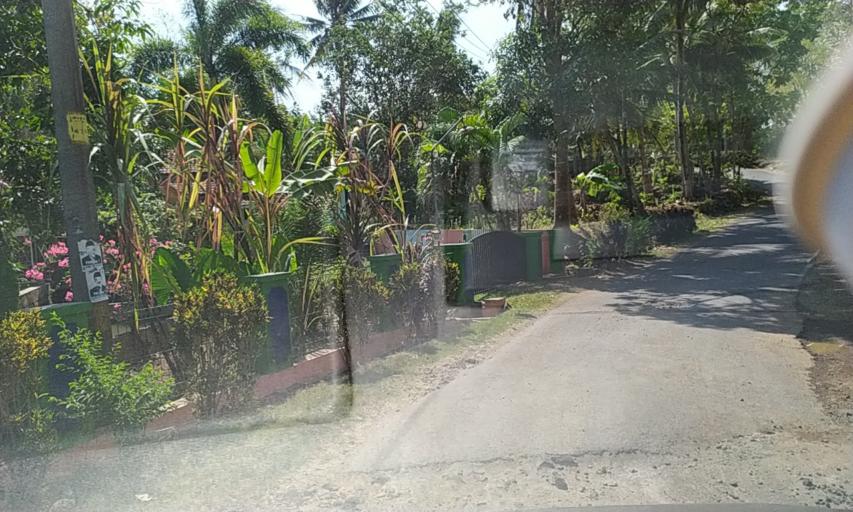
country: ID
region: Central Java
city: Cimalati
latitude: -7.2970
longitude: 108.6373
